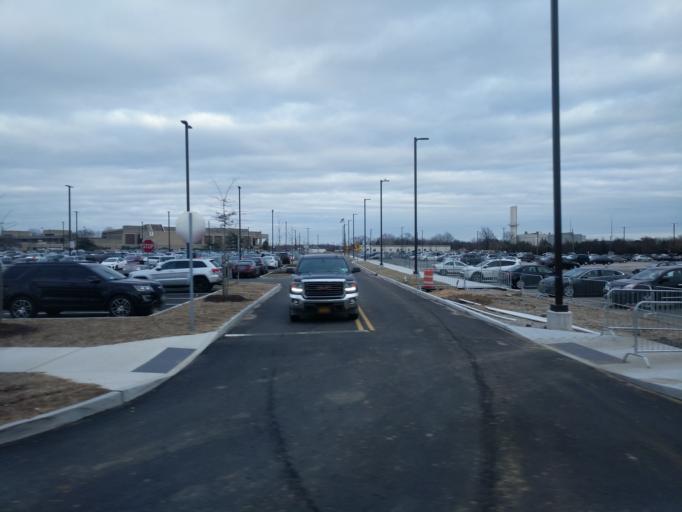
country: US
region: New York
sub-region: Nassau County
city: East Garden City
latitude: 40.7273
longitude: -73.5950
